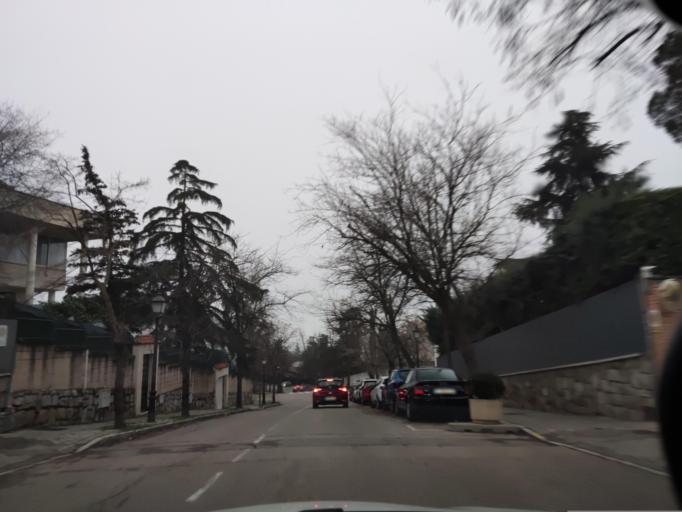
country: ES
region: Madrid
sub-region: Provincia de Madrid
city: Tetuan de las Victorias
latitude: 40.4862
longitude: -3.7095
